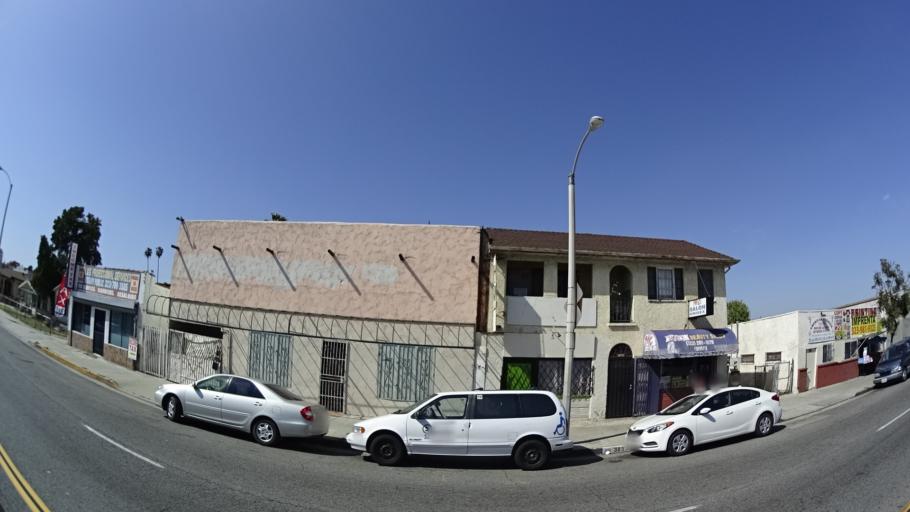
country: US
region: California
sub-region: Los Angeles County
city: Belvedere
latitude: 34.0405
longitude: -118.1830
